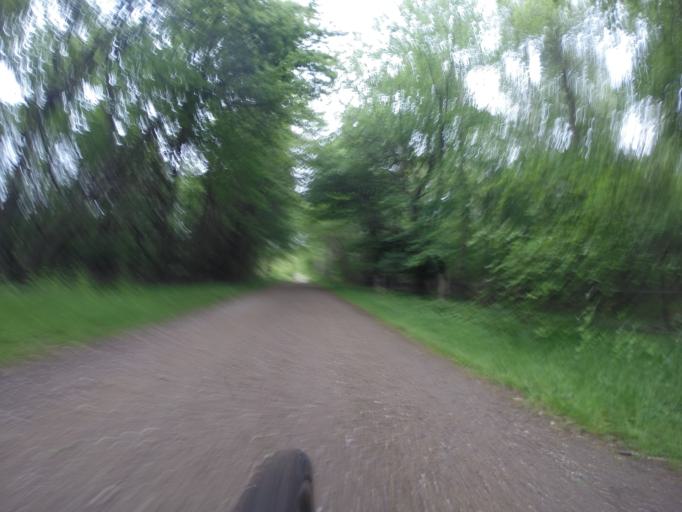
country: DK
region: Capital Region
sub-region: Ballerup Kommune
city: Ballerup
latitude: 55.6946
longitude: 12.3499
